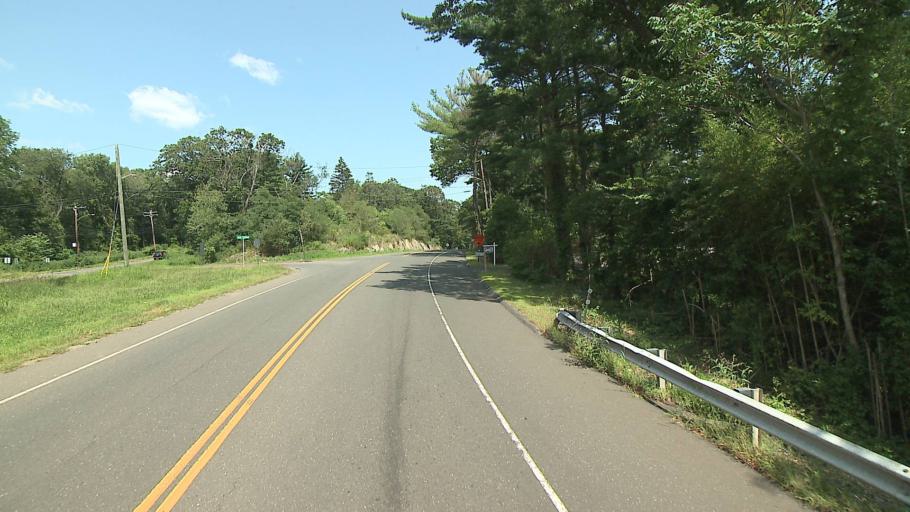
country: US
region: Connecticut
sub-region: Fairfield County
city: Stratford
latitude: 41.2264
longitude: -73.1141
